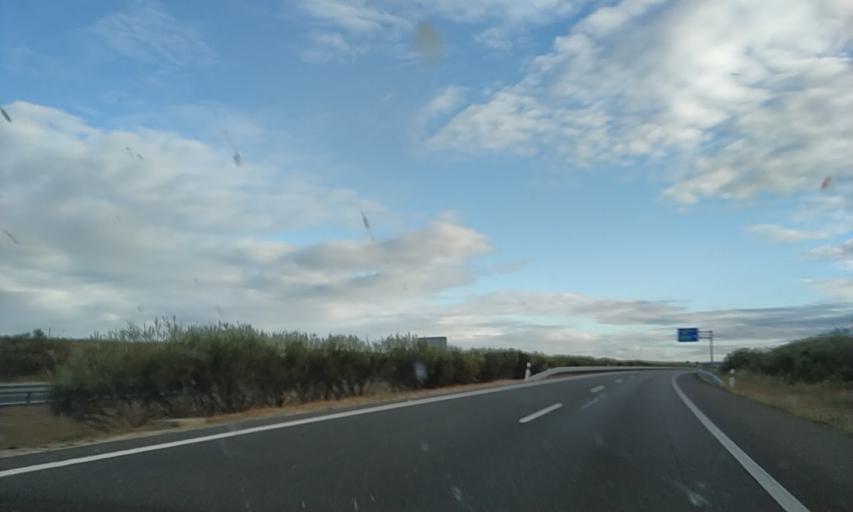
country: ES
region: Extremadura
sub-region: Provincia de Caceres
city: Casar de Caceres
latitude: 39.5440
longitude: -6.4042
